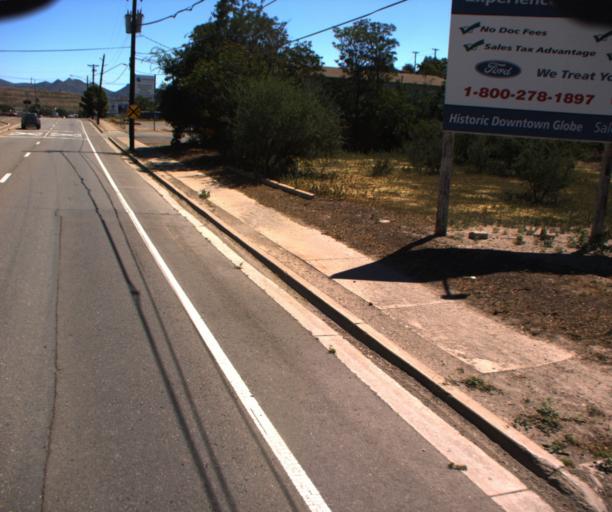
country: US
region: Arizona
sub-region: Gila County
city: Miami
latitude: 33.4051
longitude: -110.8590
